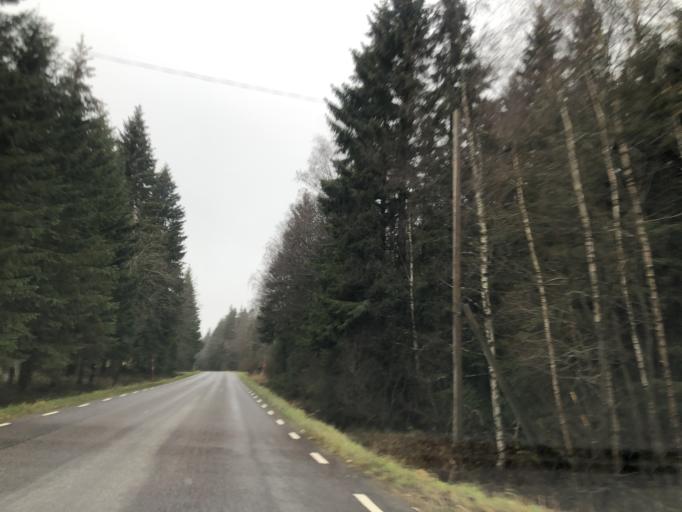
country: SE
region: Vaestra Goetaland
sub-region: Ulricehamns Kommun
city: Ulricehamn
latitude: 57.7603
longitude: 13.4885
